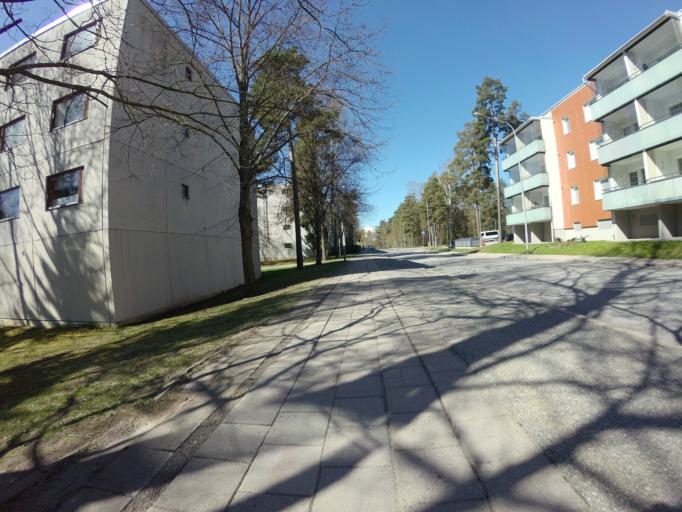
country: FI
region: Varsinais-Suomi
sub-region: Turku
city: Raisio
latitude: 60.4559
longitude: 22.1613
